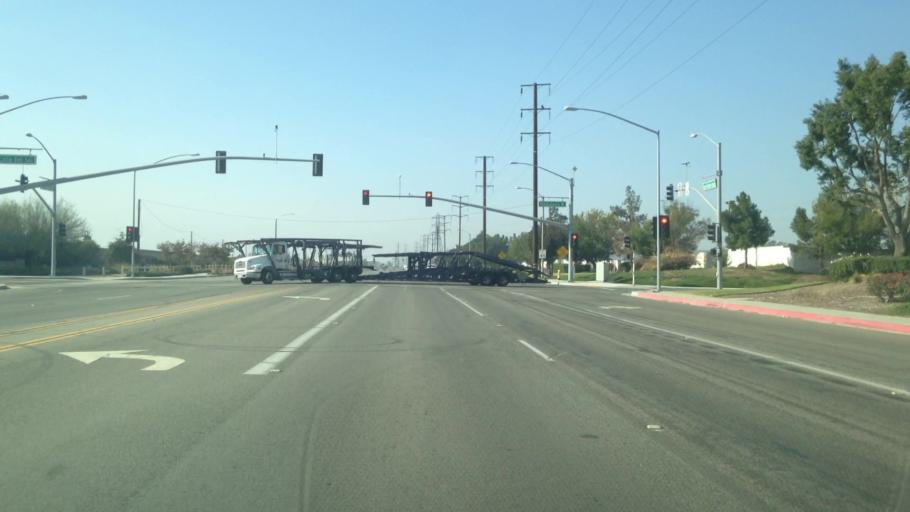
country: US
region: California
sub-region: Riverside County
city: Mira Loma
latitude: 34.0043
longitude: -117.5350
